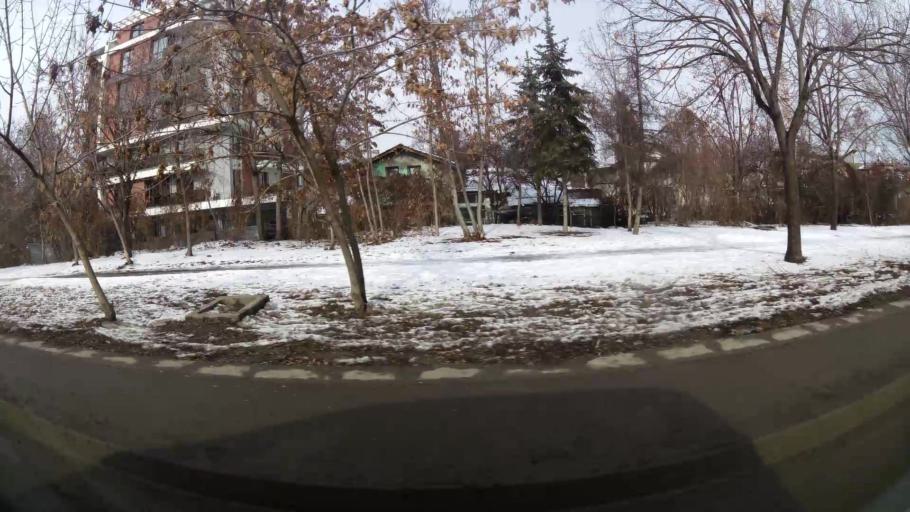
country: BG
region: Sofia-Capital
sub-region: Stolichna Obshtina
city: Sofia
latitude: 42.7014
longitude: 23.3763
